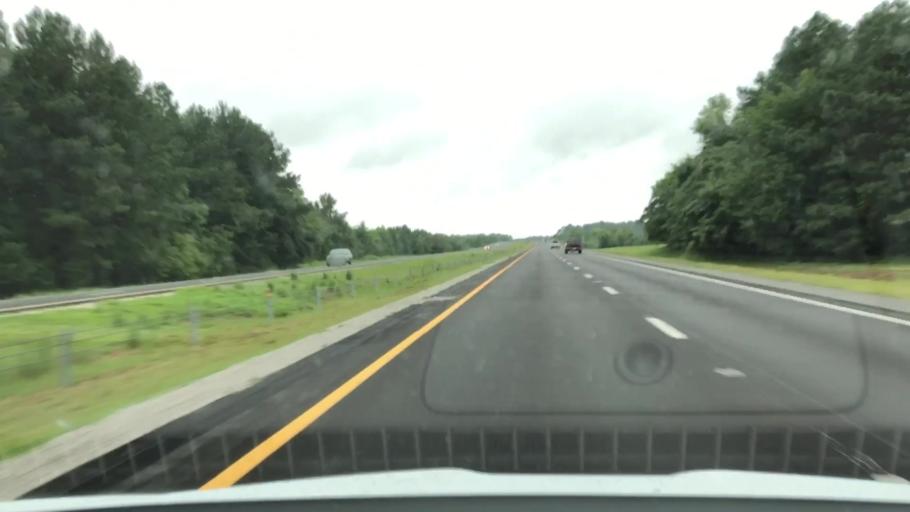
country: US
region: North Carolina
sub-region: Wayne County
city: Goldsboro
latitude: 35.4625
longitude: -77.9857
